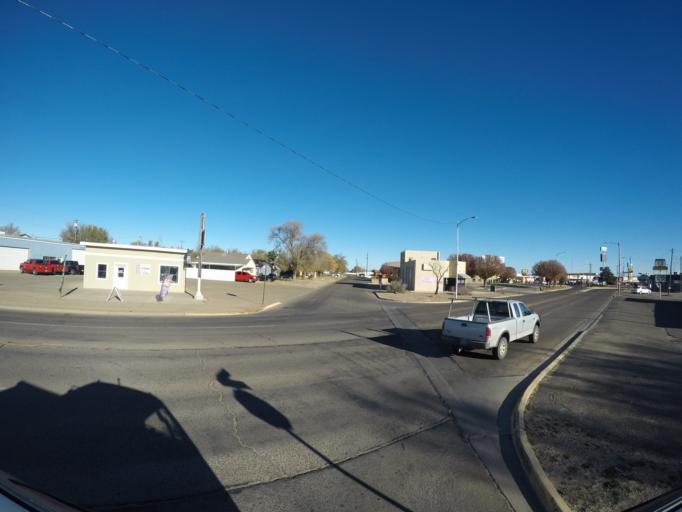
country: US
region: New Mexico
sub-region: Curry County
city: Clovis
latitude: 34.4175
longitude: -103.1977
